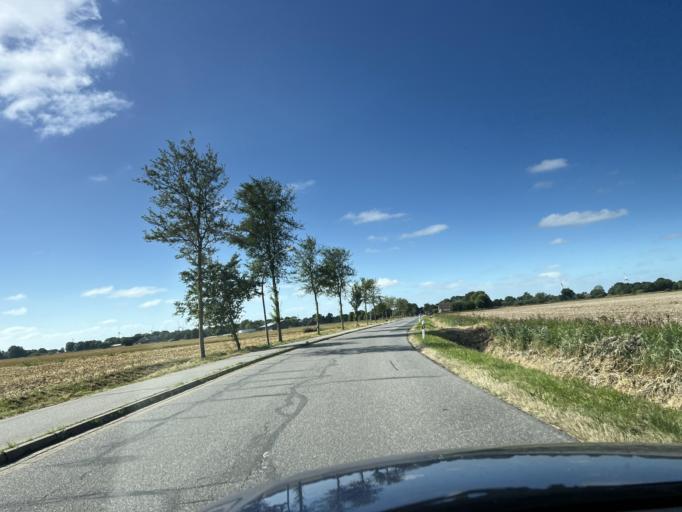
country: DE
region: Schleswig-Holstein
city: Norddeich
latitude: 54.2138
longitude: 8.9116
